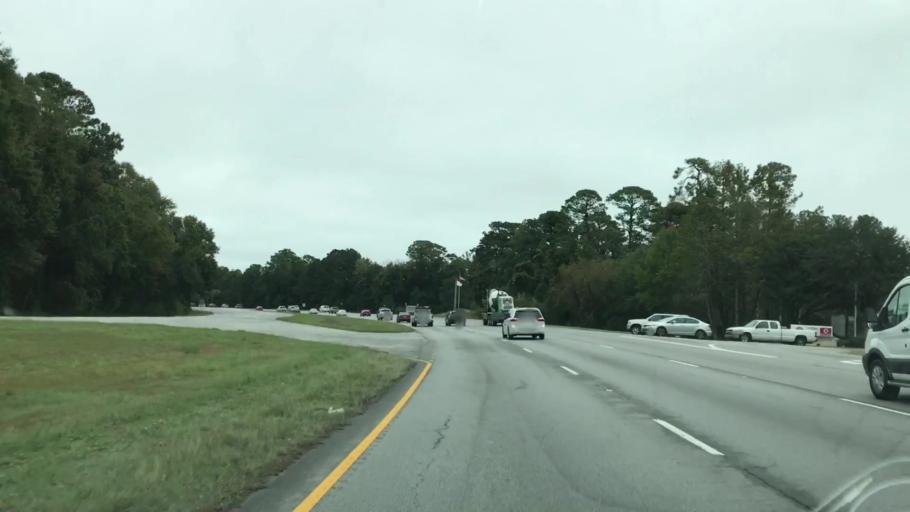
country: US
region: South Carolina
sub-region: Beaufort County
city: Bluffton
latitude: 32.2421
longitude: -80.8235
